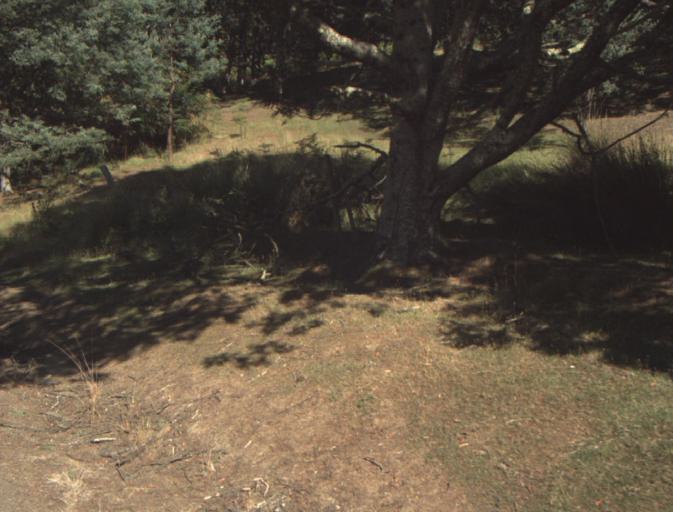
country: AU
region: Tasmania
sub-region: Dorset
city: Scottsdale
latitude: -41.2910
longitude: 147.3576
